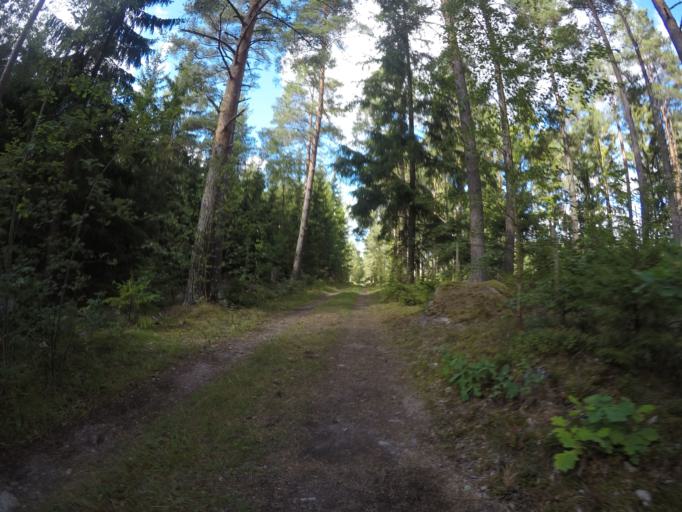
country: SE
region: Vaestmanland
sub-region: Hallstahammars Kommun
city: Kolback
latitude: 59.4932
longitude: 16.1989
